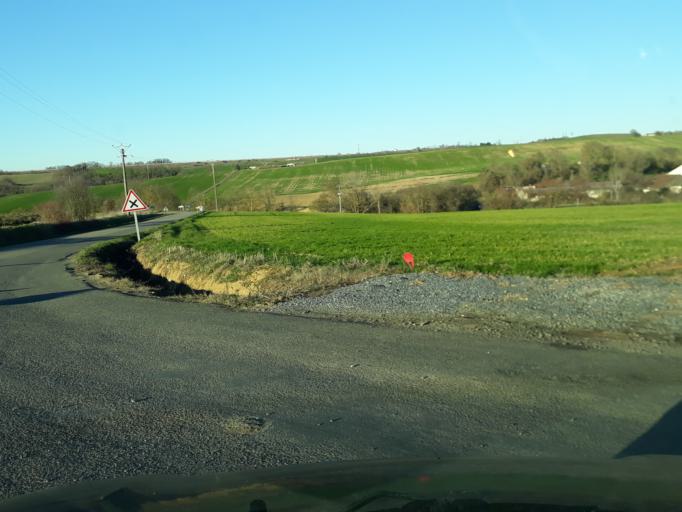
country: FR
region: Midi-Pyrenees
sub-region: Departement du Gers
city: Aubiet
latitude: 43.6357
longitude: 0.6902
